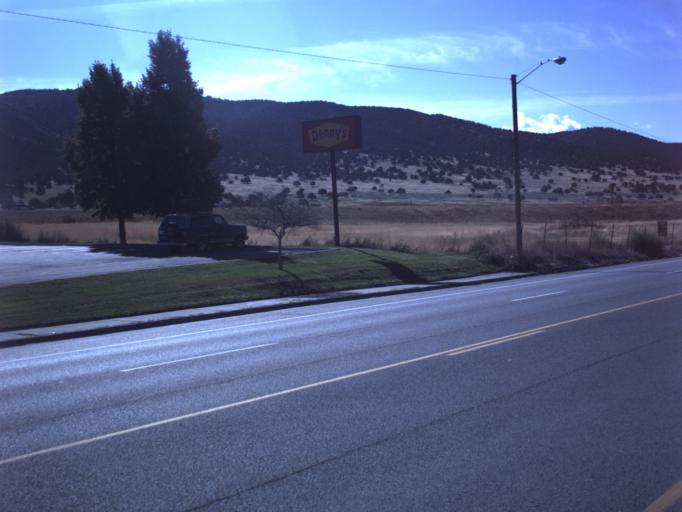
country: US
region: Utah
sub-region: Juab County
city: Nephi
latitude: 39.6852
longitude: -111.8378
